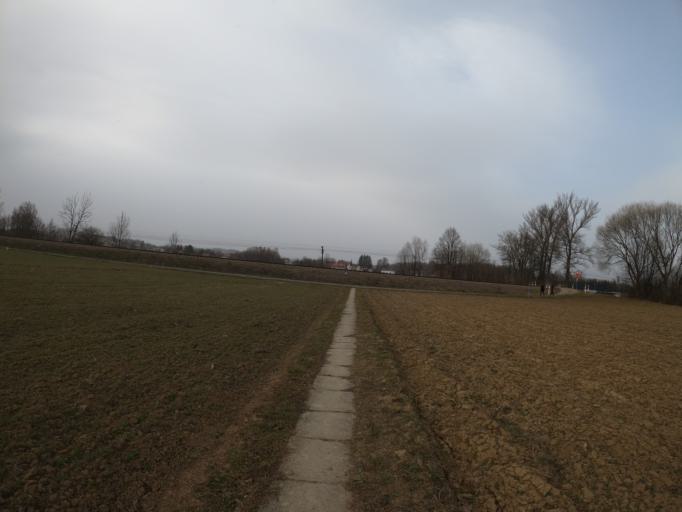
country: PL
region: Subcarpathian Voivodeship
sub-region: Powiat strzyzowski
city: Wisniowa
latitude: 49.8626
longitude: 21.6421
